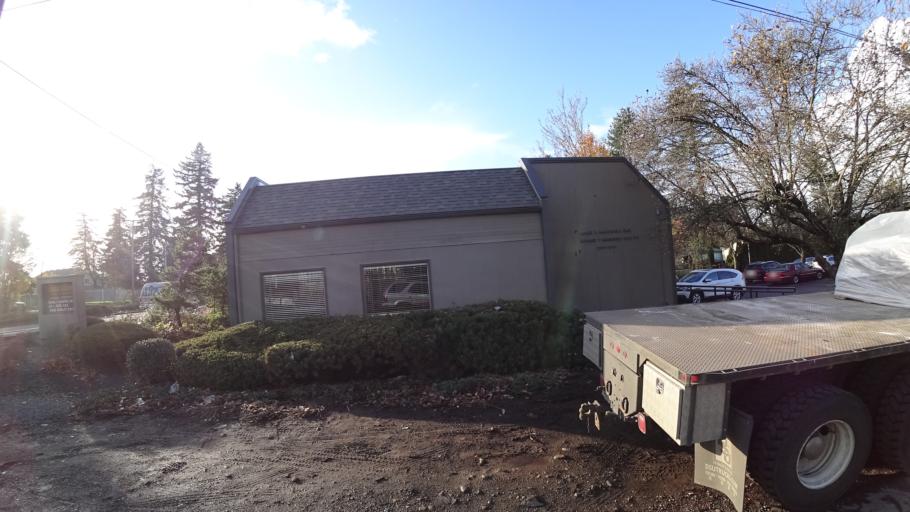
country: US
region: Oregon
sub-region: Multnomah County
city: Lents
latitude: 45.5228
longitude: -122.5392
